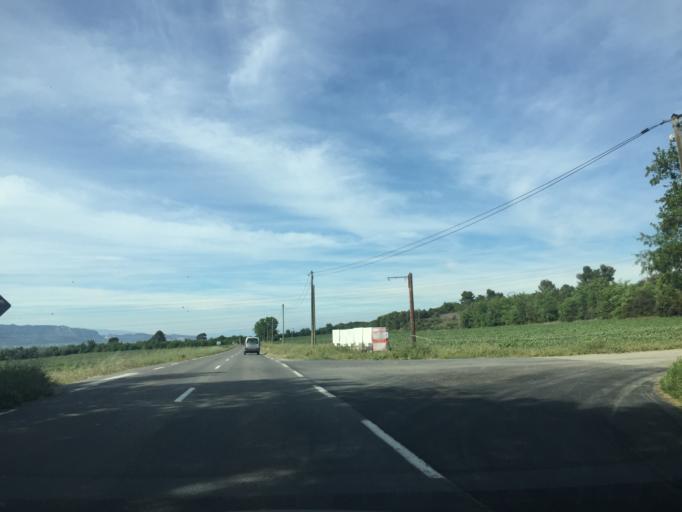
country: FR
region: Provence-Alpes-Cote d'Azur
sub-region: Departement du Var
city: Vinon-sur-Verdon
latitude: 43.7713
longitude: 5.8134
